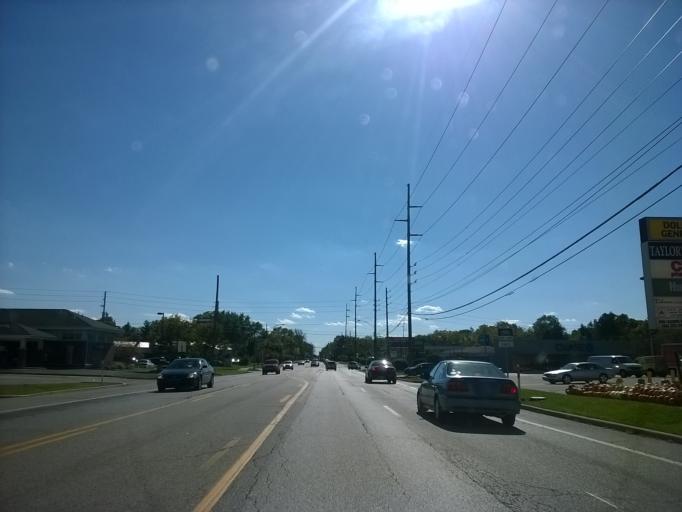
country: US
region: Indiana
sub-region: Marion County
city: Broad Ripple
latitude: 39.8697
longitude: -86.0965
